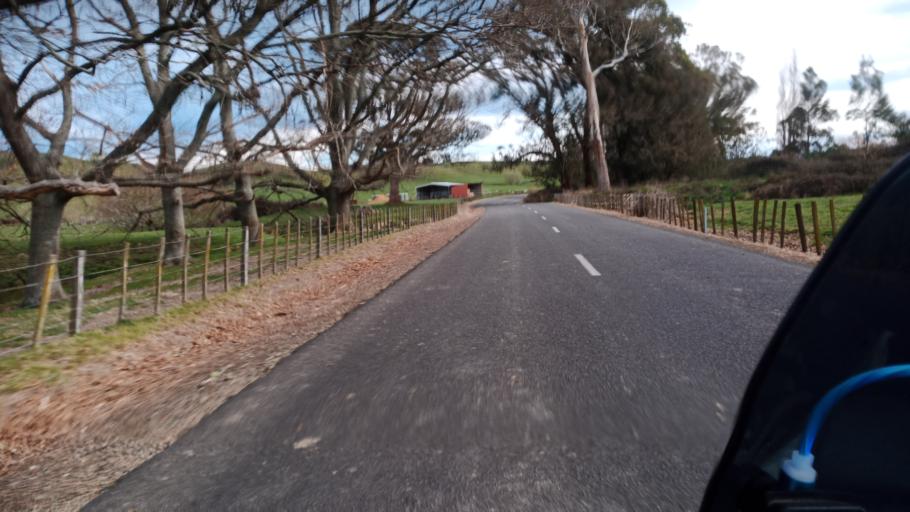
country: NZ
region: Hawke's Bay
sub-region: Wairoa District
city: Wairoa
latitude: -38.9754
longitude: 177.4247
